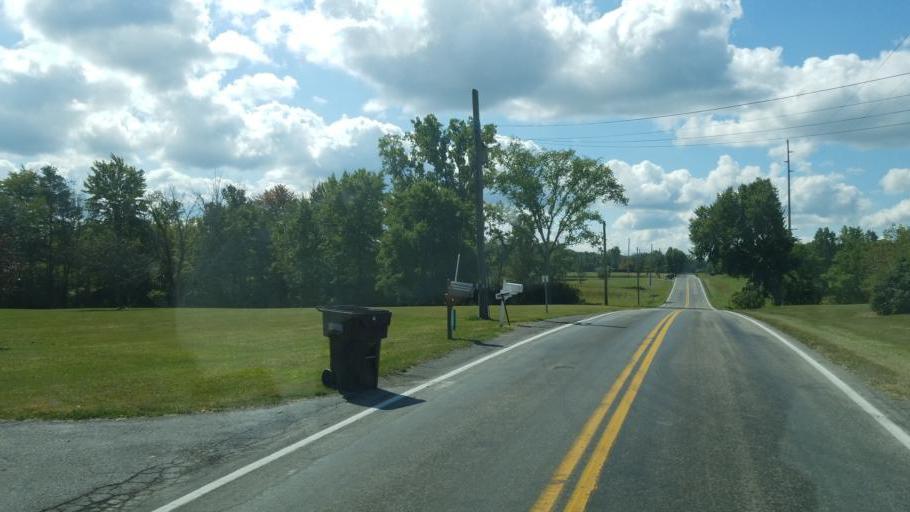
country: US
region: Ohio
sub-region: Lorain County
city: Lagrange
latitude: 41.1843
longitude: -82.1085
